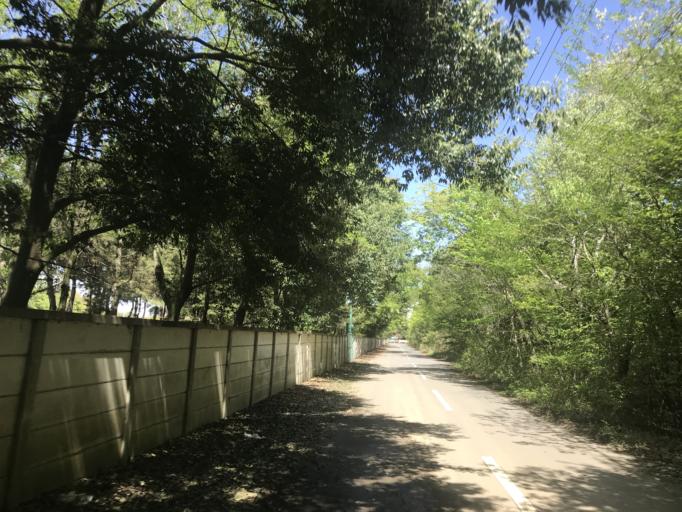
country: JP
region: Ibaraki
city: Shimodate
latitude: 36.2878
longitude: 140.0187
